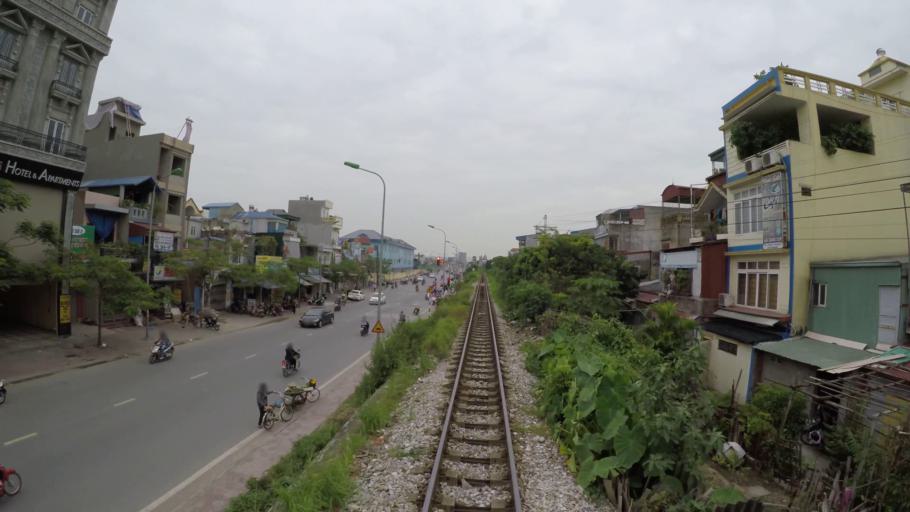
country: VN
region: Hai Phong
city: An Duong
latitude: 20.8728
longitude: 106.6460
